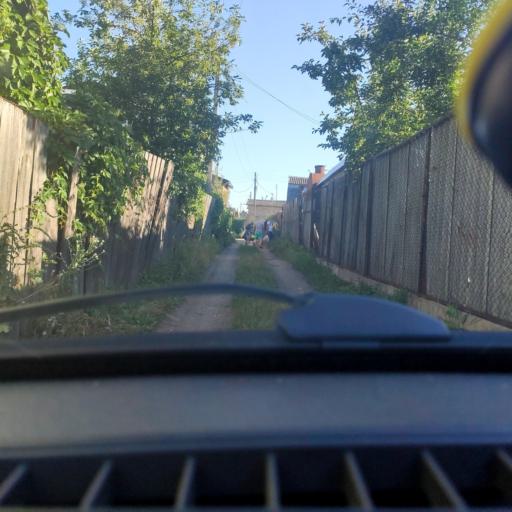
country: RU
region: Samara
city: Zhigulevsk
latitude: 53.5018
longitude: 49.5038
